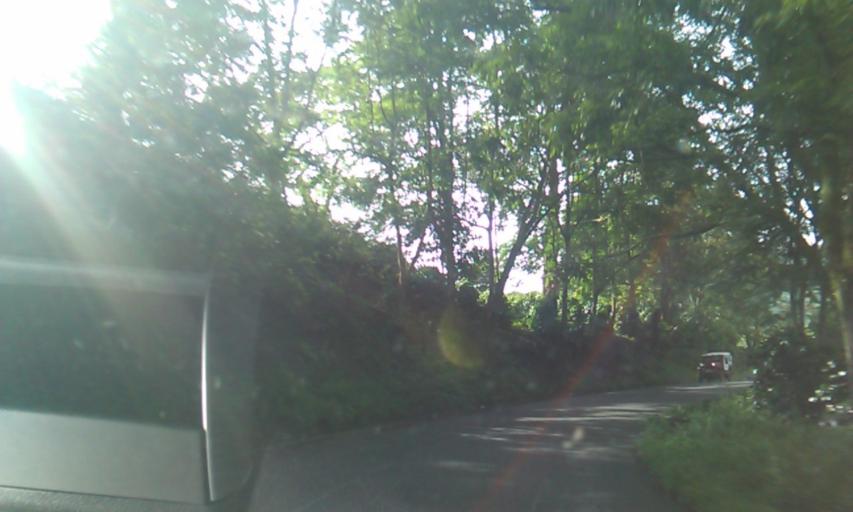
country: CO
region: Quindio
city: Cordoba
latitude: 4.4019
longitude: -75.6895
